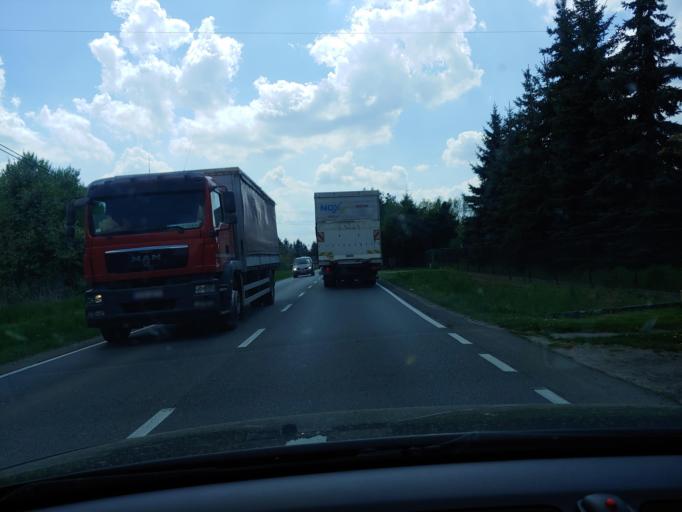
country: PL
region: Lesser Poland Voivodeship
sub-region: Powiat tarnowski
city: Lisia Gora
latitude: 50.0622
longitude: 21.0137
